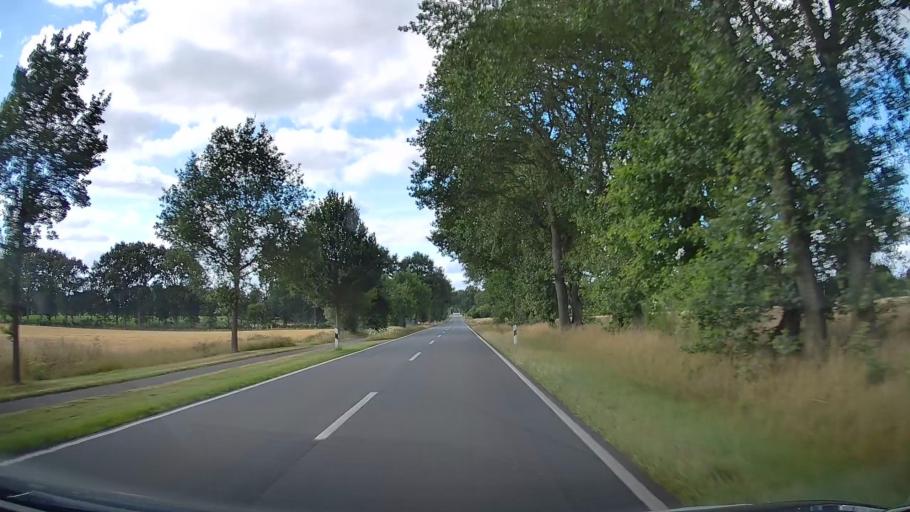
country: DE
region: Lower Saxony
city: Vrees
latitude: 52.9025
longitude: 7.8408
